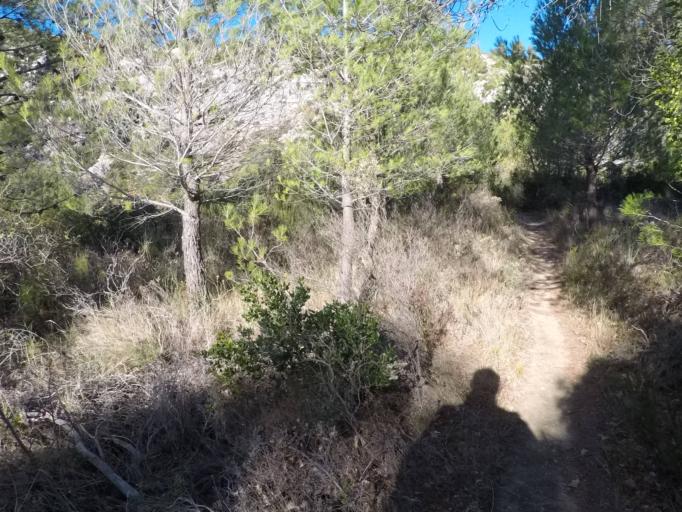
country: FR
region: Provence-Alpes-Cote d'Azur
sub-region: Departement des Bouches-du-Rhone
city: La Penne-sur-Huveaune
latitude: 43.2682
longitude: 5.4993
